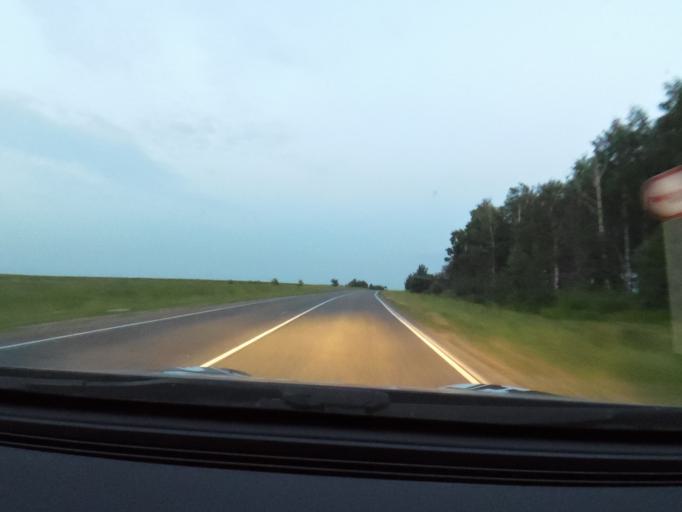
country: RU
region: Bashkortostan
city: Duvan
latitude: 56.1173
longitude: 58.0431
